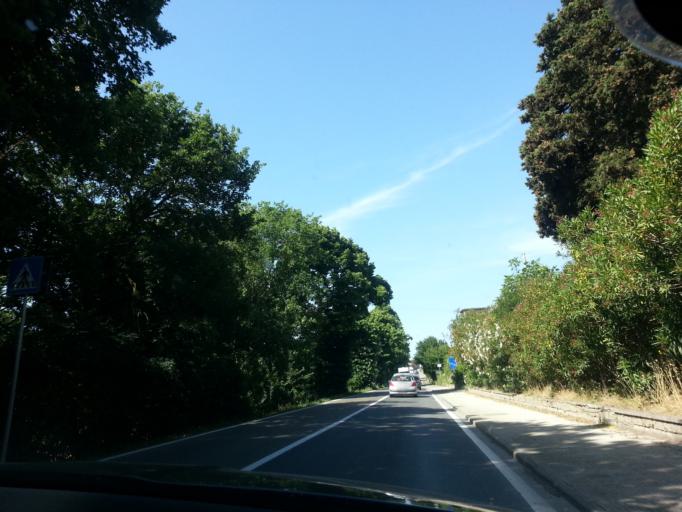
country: IT
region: Latium
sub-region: Provincia di Viterbo
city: Monte Romano
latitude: 42.2735
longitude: 11.9079
